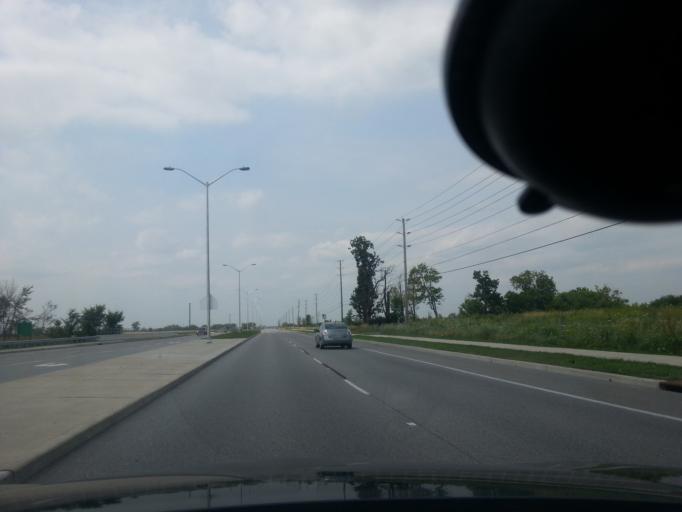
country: CA
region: Ontario
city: Ottawa
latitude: 45.2905
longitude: -75.6727
